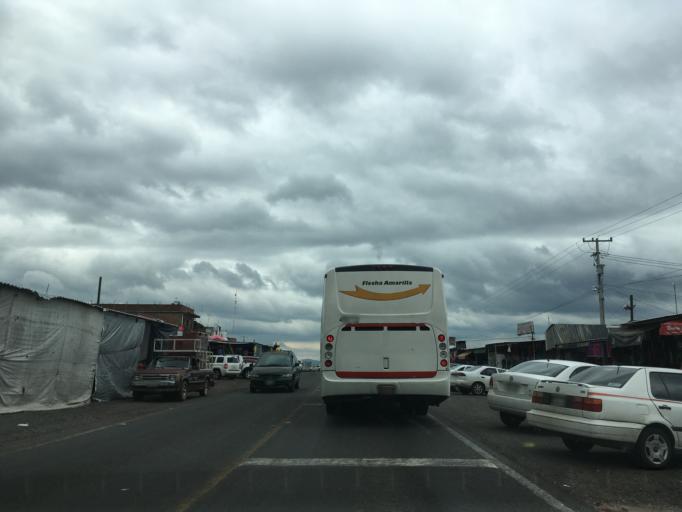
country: MX
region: Michoacan
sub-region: Cuitzeo
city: Cuamio
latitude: 20.0577
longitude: -101.1502
